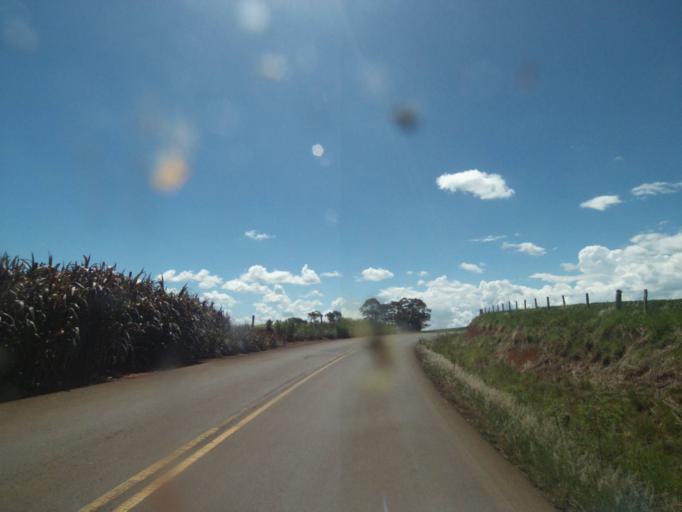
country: BR
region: Parana
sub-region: Pinhao
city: Pinhao
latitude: -25.8130
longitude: -52.0665
